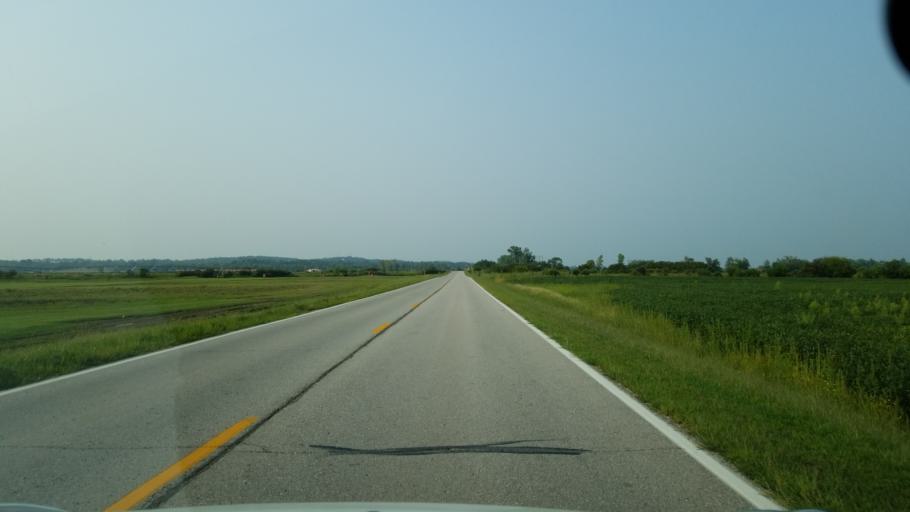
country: US
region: Nebraska
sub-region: Sarpy County
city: Bellevue
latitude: 41.1056
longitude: -95.8899
